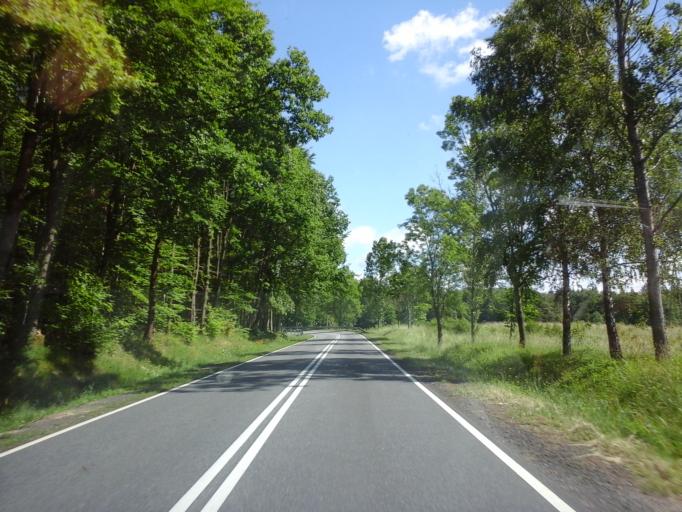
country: PL
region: West Pomeranian Voivodeship
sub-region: Powiat stargardzki
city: Insko
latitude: 53.4793
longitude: 15.5812
